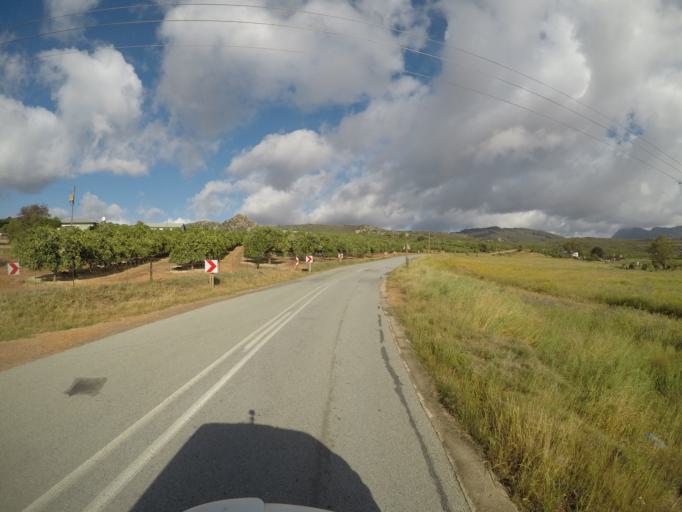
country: ZA
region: Western Cape
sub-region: West Coast District Municipality
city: Clanwilliam
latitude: -32.4383
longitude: 18.9424
